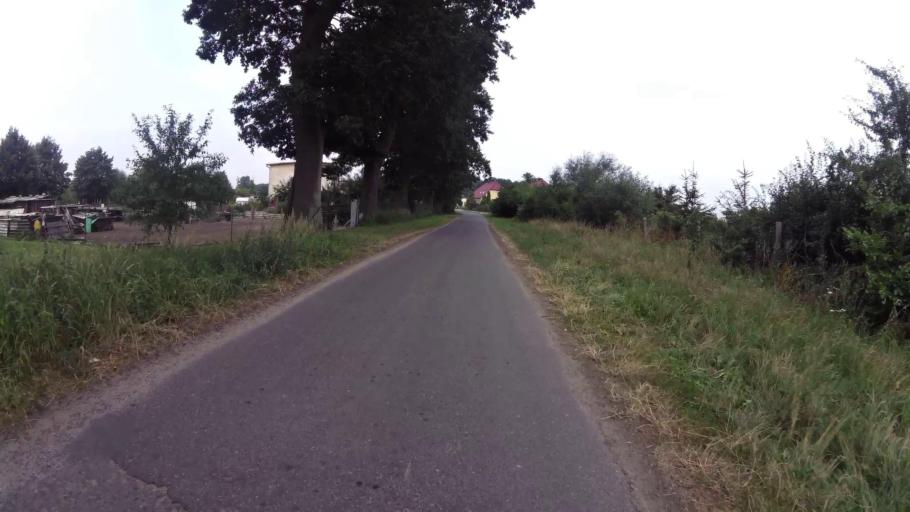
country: PL
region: West Pomeranian Voivodeship
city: Trzcinsko Zdroj
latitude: 52.9055
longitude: 14.6616
